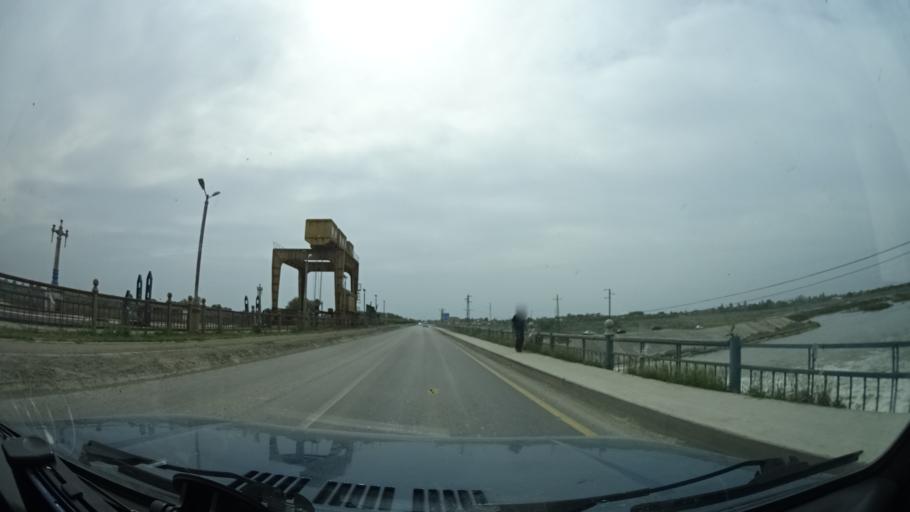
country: IR
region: Ardabil
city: Parsabad
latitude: 39.7391
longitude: 47.9734
